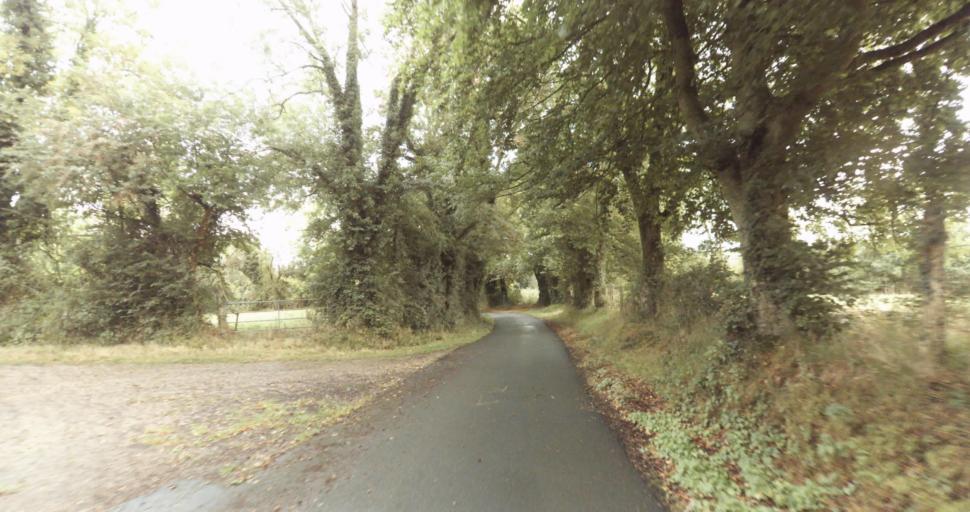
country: FR
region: Lower Normandy
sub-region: Departement de l'Orne
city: Vimoutiers
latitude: 48.9101
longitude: 0.1655
